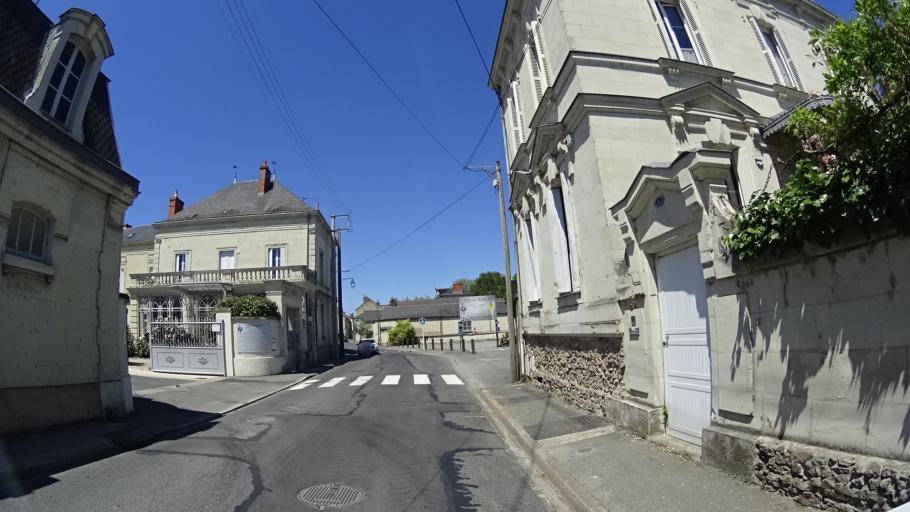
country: FR
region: Pays de la Loire
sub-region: Departement de Maine-et-Loire
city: Saumur
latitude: 47.2681
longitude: -0.1026
